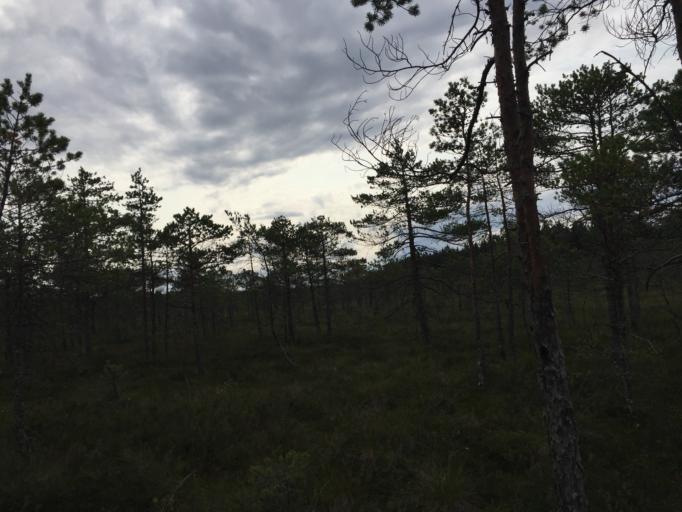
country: LV
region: Pargaujas
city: Stalbe
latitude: 57.3163
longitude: 25.0514
